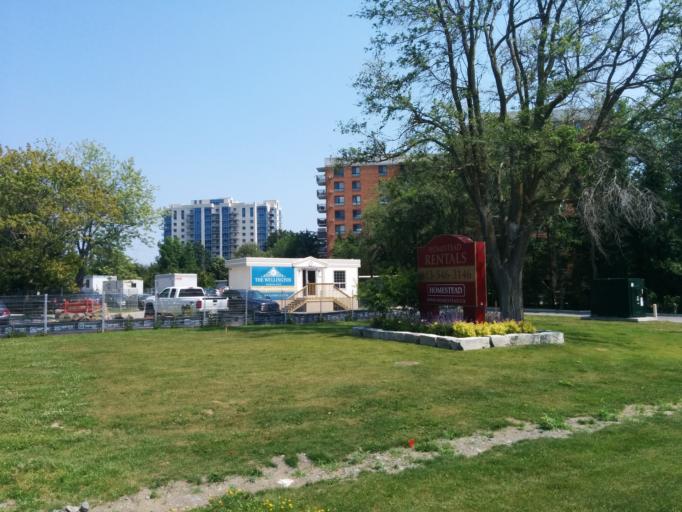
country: CA
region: Ontario
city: Kingston
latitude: 44.2514
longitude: -76.4607
